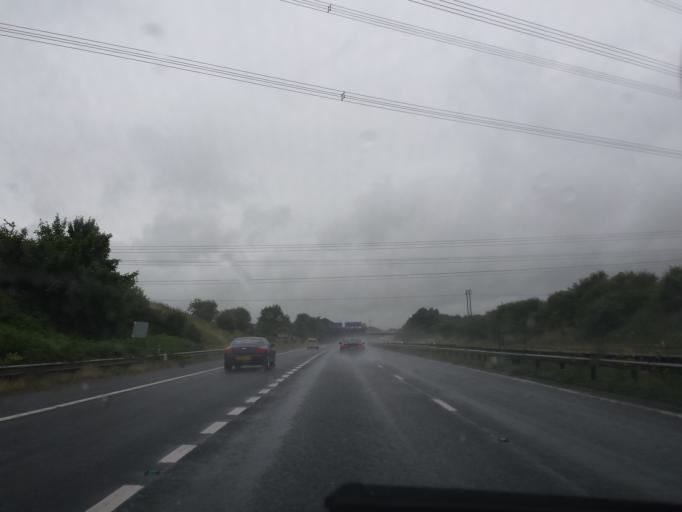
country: GB
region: England
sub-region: Rotherham
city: Bramley
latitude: 53.4038
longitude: -1.2622
